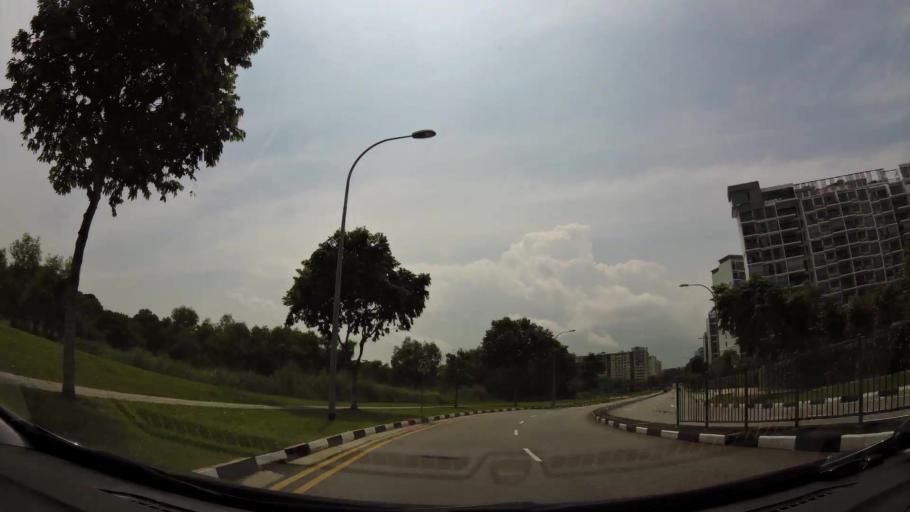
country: MY
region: Johor
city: Kampung Pasir Gudang Baru
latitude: 1.3786
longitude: 103.9621
